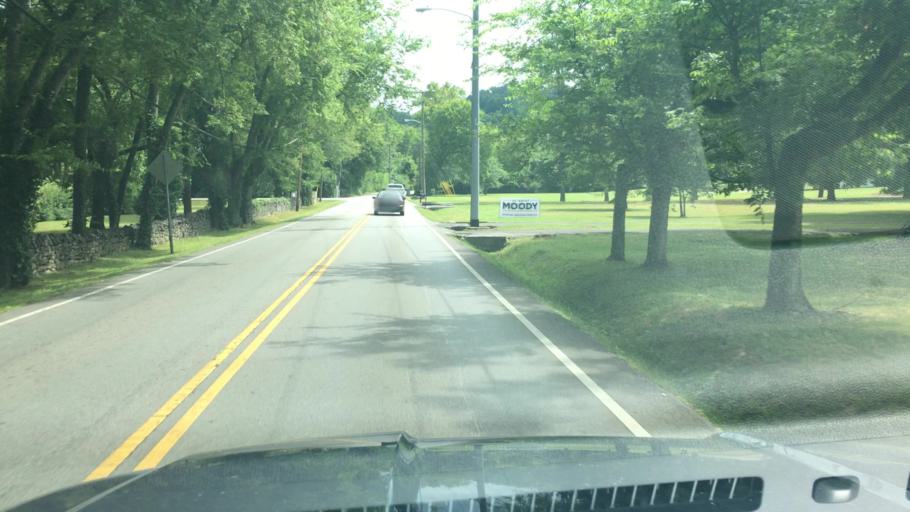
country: US
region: Tennessee
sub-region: Davidson County
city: Oak Hill
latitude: 36.0796
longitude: -86.8056
